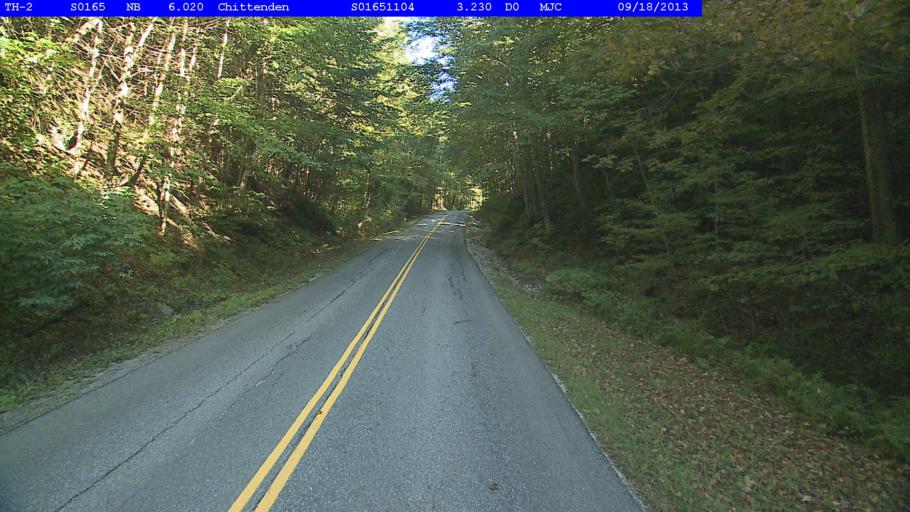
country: US
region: Vermont
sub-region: Rutland County
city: Rutland
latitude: 43.7213
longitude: -72.9662
